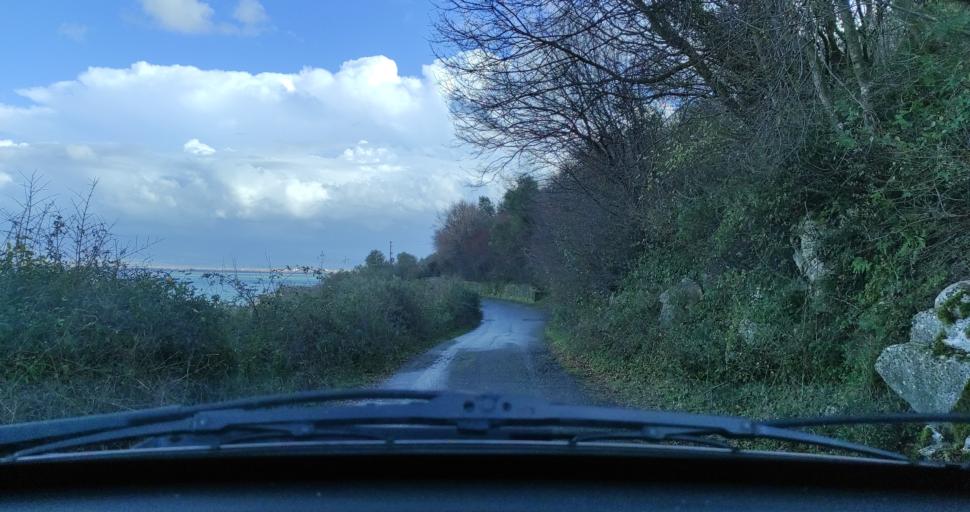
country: AL
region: Shkoder
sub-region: Rrethi i Shkodres
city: Dajc
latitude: 42.0694
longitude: 19.4077
